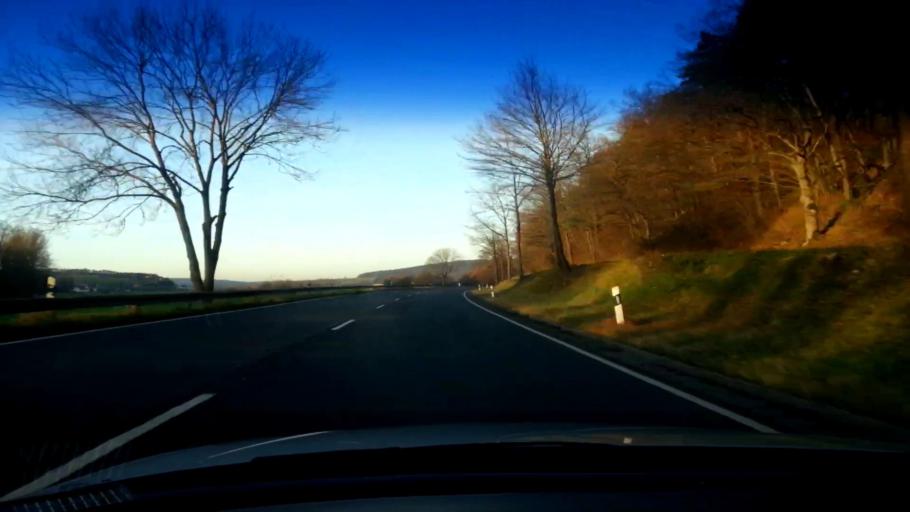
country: DE
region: Bavaria
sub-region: Upper Franconia
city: Rattelsdorf
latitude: 50.0359
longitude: 10.8825
